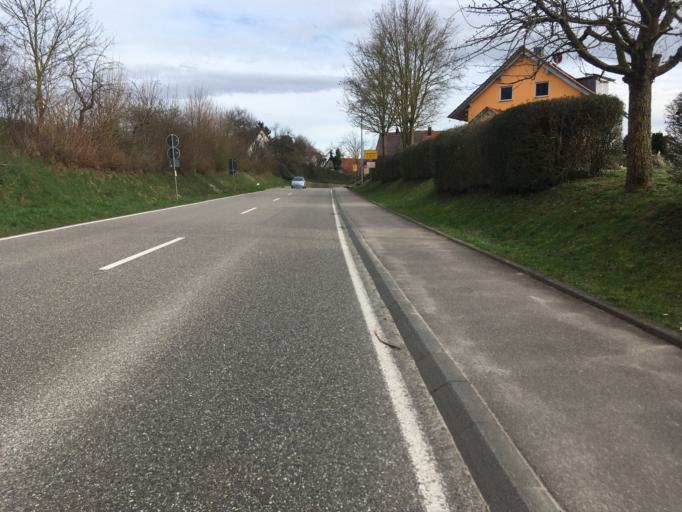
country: DE
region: Baden-Wuerttemberg
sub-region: Regierungsbezirk Stuttgart
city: Bretzfeld
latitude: 49.2176
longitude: 9.4038
